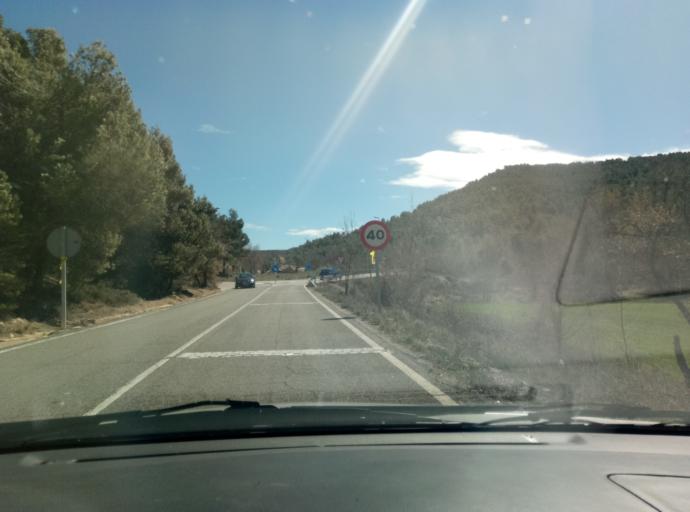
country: ES
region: Catalonia
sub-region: Provincia de Lleida
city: Nalec
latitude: 41.5084
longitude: 1.1350
